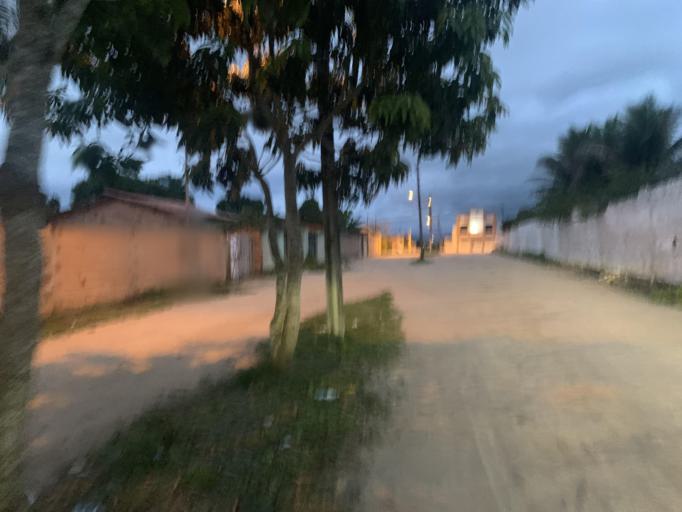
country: BR
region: Bahia
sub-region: Medeiros Neto
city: Medeiros Neto
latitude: -17.3891
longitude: -40.2339
